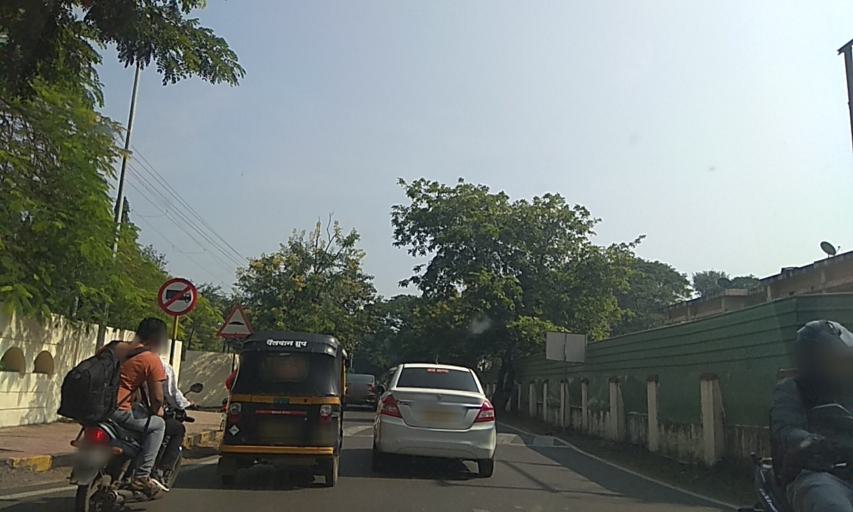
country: IN
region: Maharashtra
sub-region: Pune Division
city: Khadki
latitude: 18.5578
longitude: 73.8498
